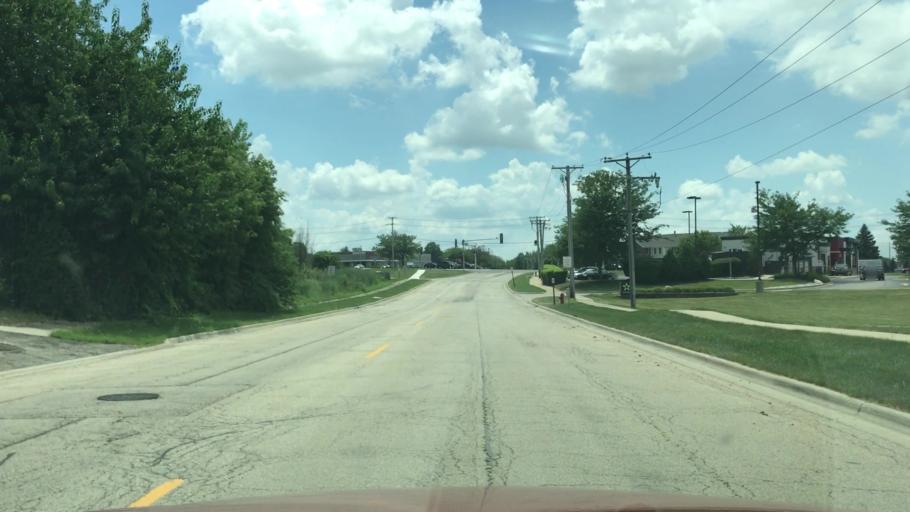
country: US
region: Illinois
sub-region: DuPage County
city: Hanover Park
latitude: 41.9786
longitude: -88.1299
